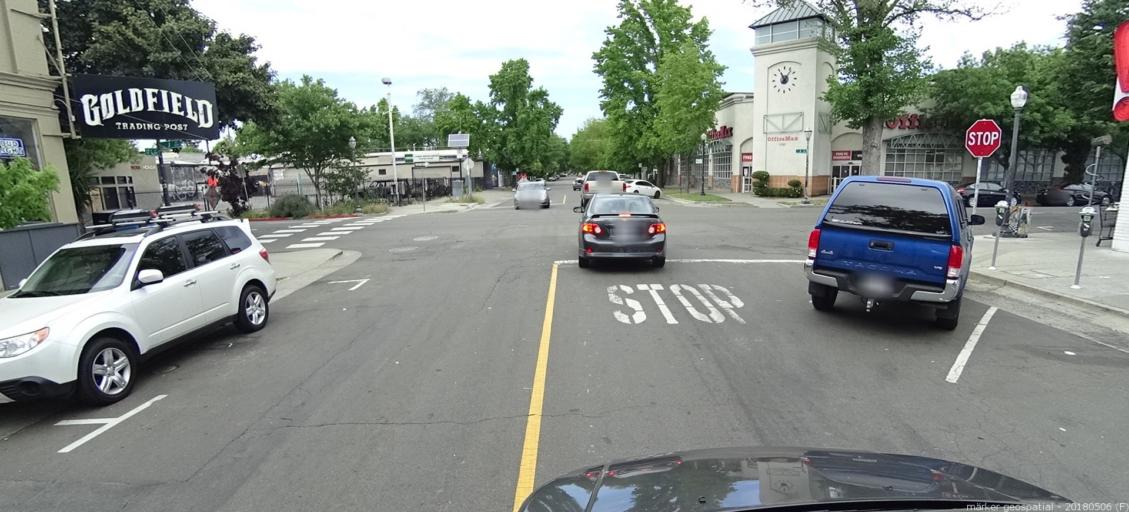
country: US
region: California
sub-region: Sacramento County
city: Sacramento
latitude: 38.5776
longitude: -121.4840
